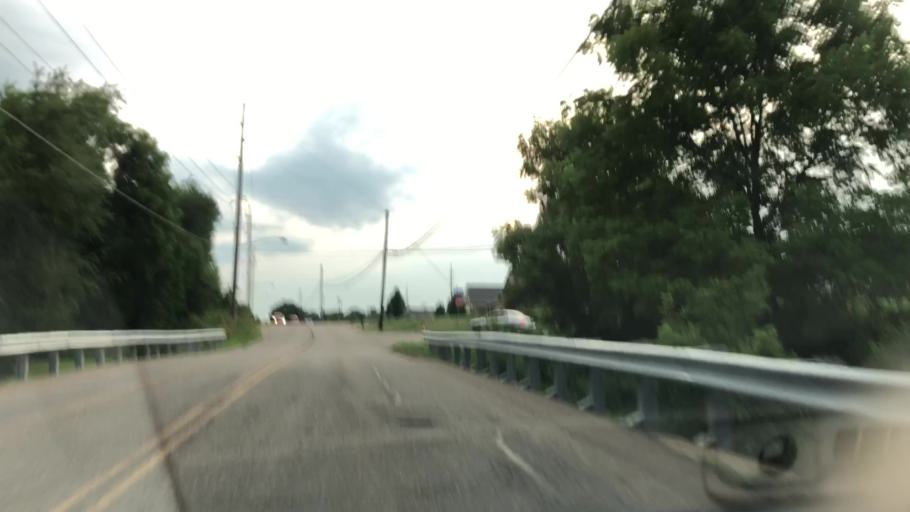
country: US
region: Ohio
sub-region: Stark County
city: Massillon
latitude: 40.8093
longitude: -81.4987
